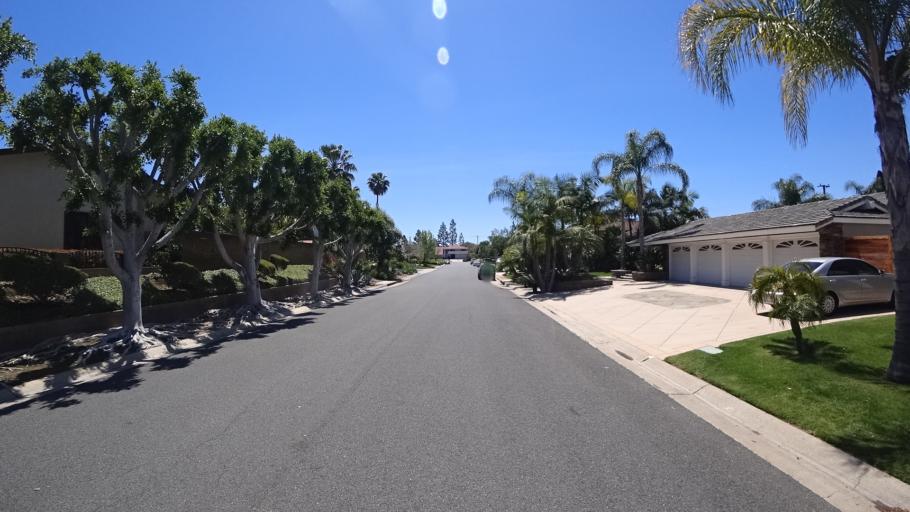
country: US
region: California
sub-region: Orange County
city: Villa Park
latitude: 33.8125
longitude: -117.8194
